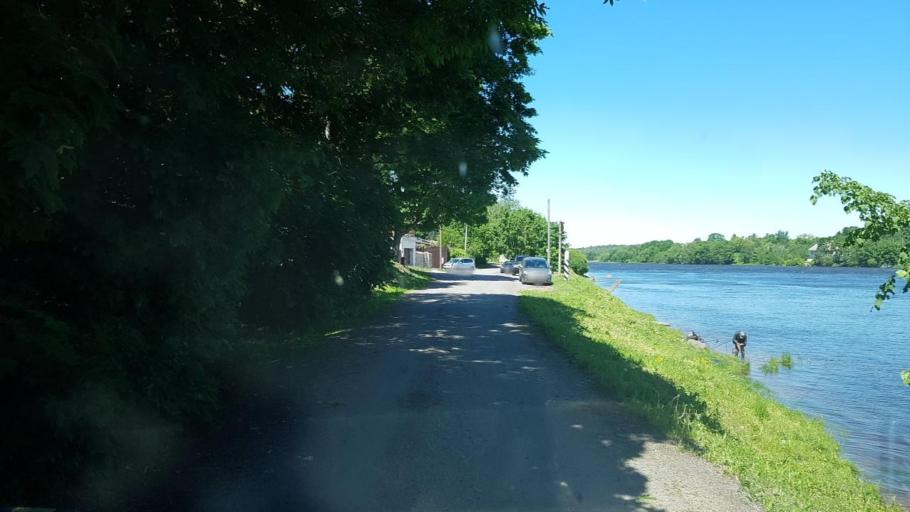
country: EE
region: Ida-Virumaa
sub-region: Narva linn
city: Narva
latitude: 59.3859
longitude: 28.2034
